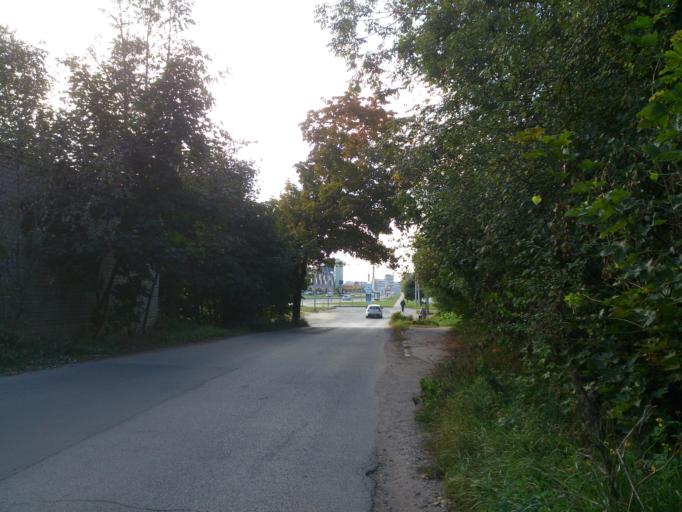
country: LT
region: Kauno apskritis
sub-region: Kaunas
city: Aleksotas
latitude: 54.8750
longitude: 23.9156
